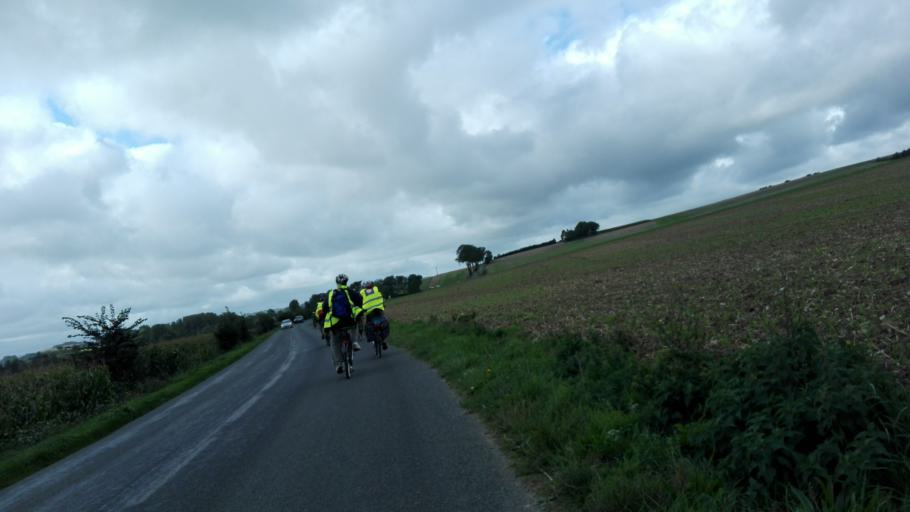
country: FR
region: Nord-Pas-de-Calais
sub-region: Departement du Pas-de-Calais
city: Licques
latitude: 50.7899
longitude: 1.9809
